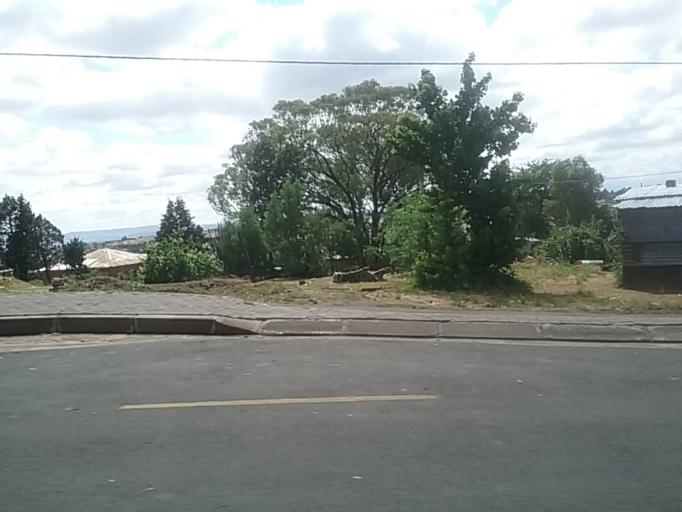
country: LS
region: Berea
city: Teyateyaneng
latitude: -29.1419
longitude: 27.7376
